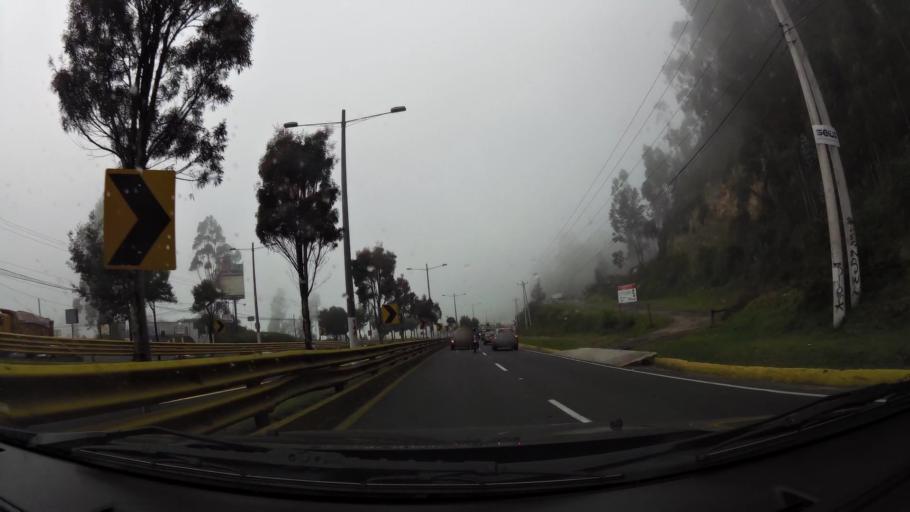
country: EC
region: Pichincha
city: Quito
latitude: -0.2571
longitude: -78.4852
